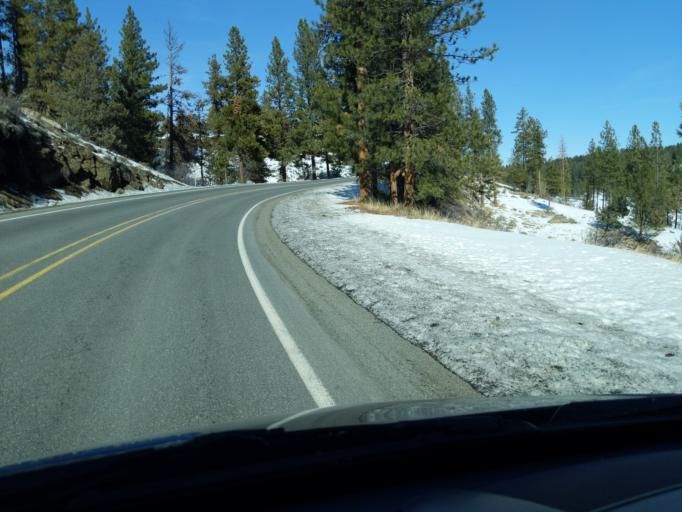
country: US
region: Oregon
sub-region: Grant County
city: John Day
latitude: 44.9069
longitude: -119.0111
